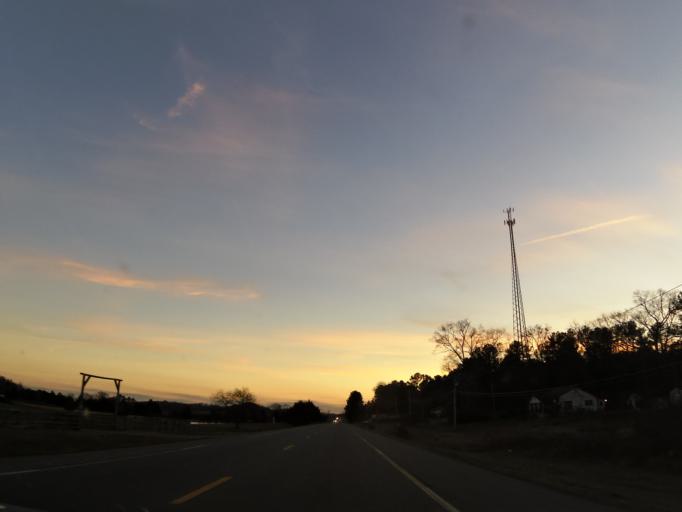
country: US
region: Tennessee
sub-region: Bradley County
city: Wildwood Lake
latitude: 35.0691
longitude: -84.8945
